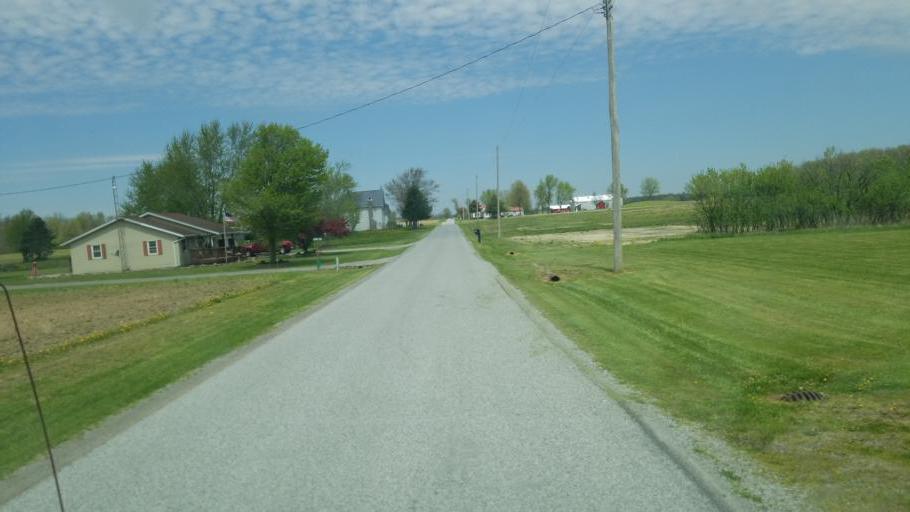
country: US
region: Ohio
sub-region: Hardin County
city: Ada
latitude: 40.8011
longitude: -83.8990
